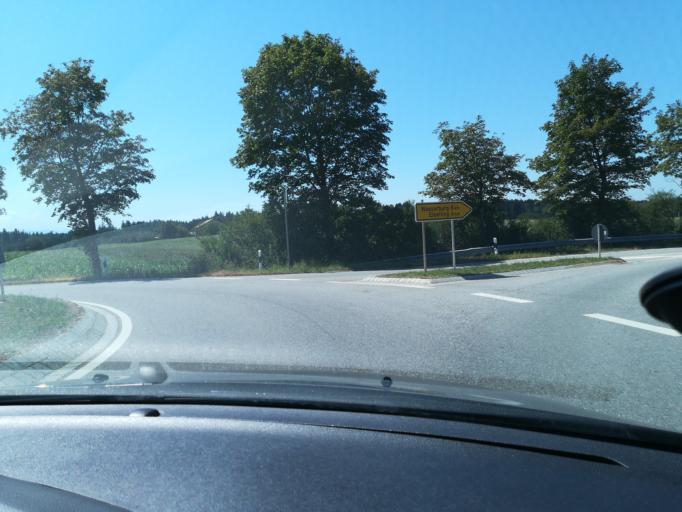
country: DE
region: Bavaria
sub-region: Upper Bavaria
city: Amerang
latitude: 48.0210
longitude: 12.2899
